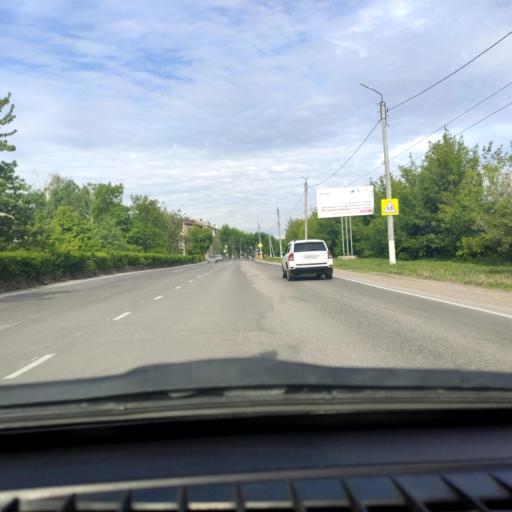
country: RU
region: Samara
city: Zhigulevsk
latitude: 53.4037
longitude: 49.5005
